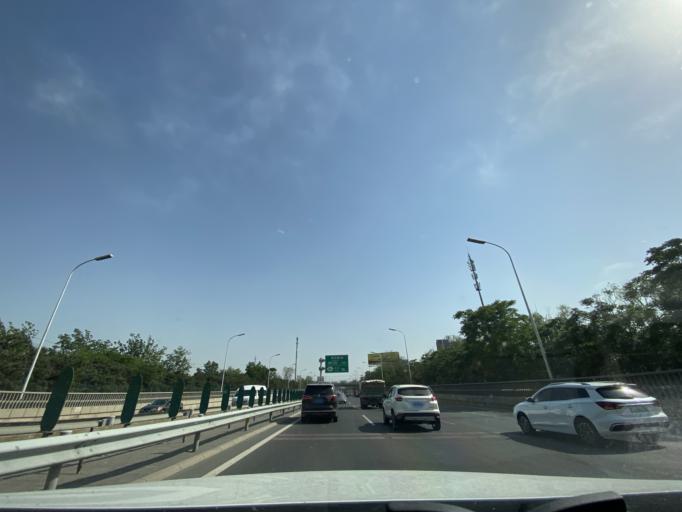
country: CN
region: Beijing
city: Lugu
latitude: 39.9349
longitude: 116.2059
